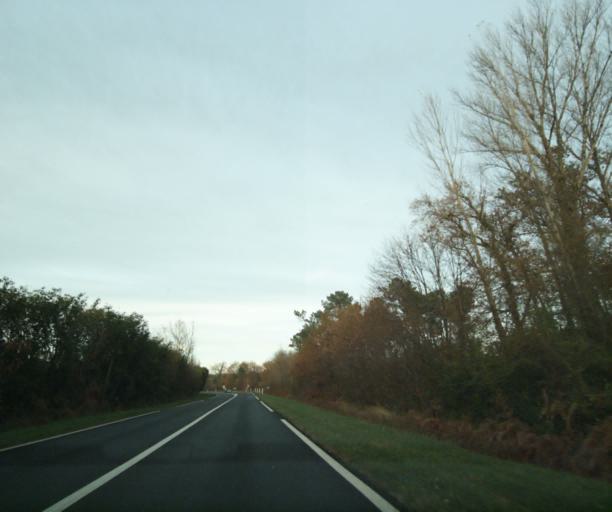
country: FR
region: Aquitaine
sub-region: Departement de la Gironde
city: Bazas
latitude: 44.3349
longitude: -0.2352
